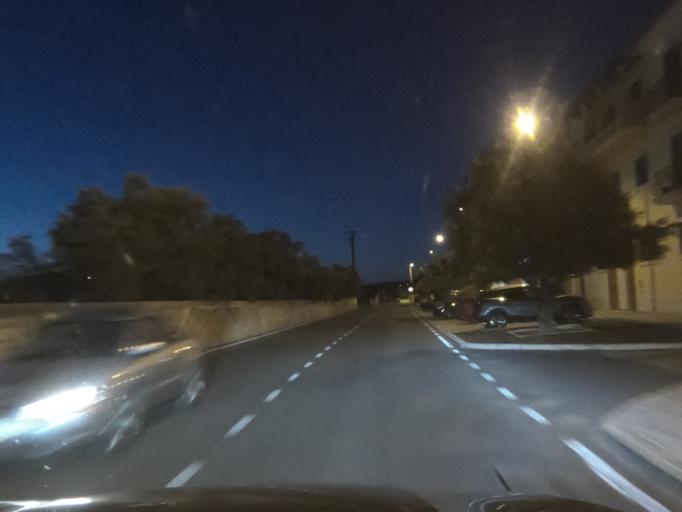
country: PT
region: Faro
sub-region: Loule
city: Loule
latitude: 37.1377
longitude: -8.0078
